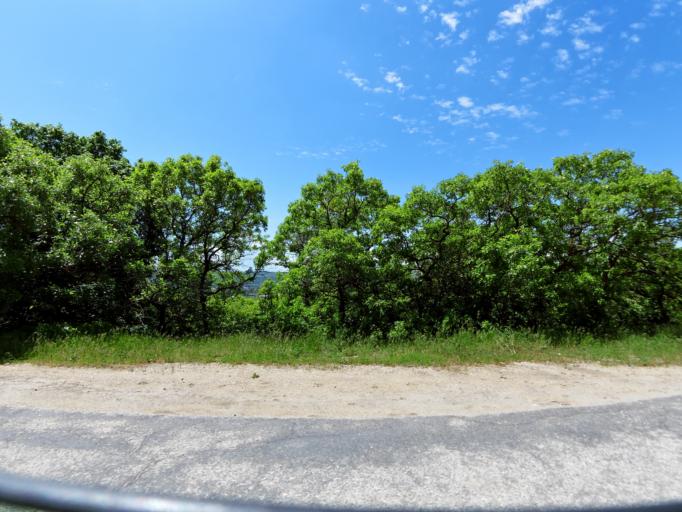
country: US
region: Utah
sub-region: Weber County
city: Uintah
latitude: 41.1633
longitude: -111.9183
